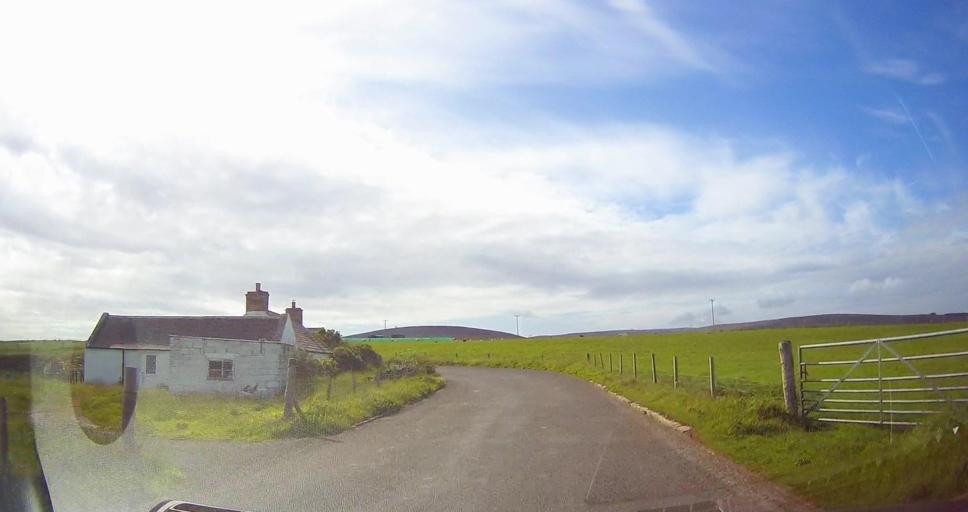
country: GB
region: Scotland
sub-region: Orkney Islands
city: Stromness
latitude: 58.8070
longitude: -3.2095
